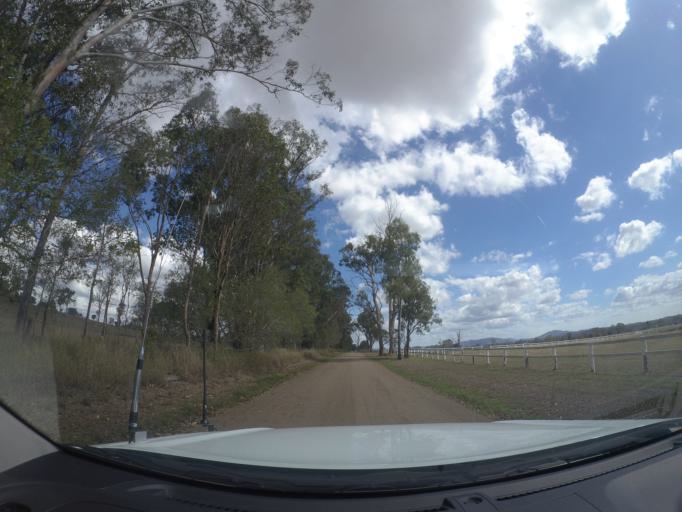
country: AU
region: Queensland
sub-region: Logan
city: Cedar Vale
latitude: -27.8862
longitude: 152.9604
